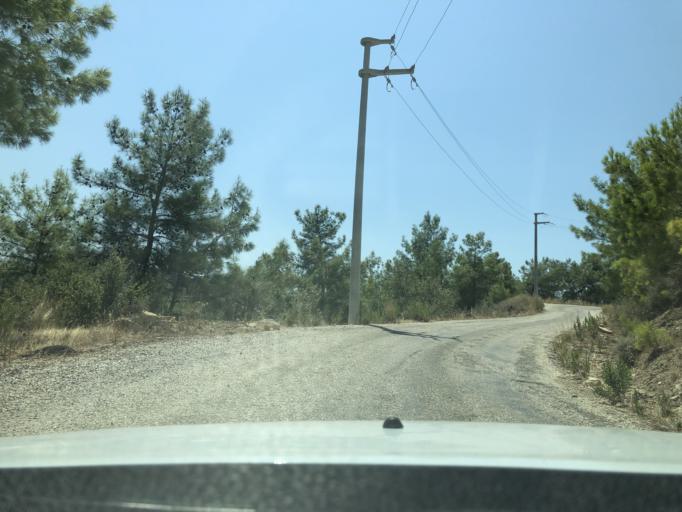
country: TR
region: Antalya
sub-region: Manavgat
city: Manavgat
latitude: 36.8708
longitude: 31.5549
